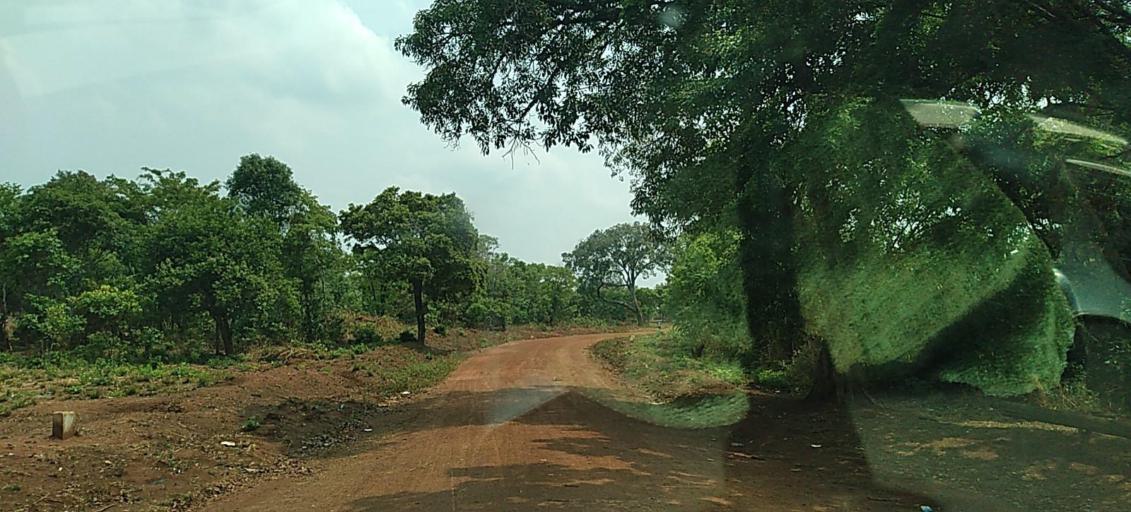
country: ZM
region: North-Western
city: Mwinilunga
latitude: -11.7246
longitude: 24.5677
